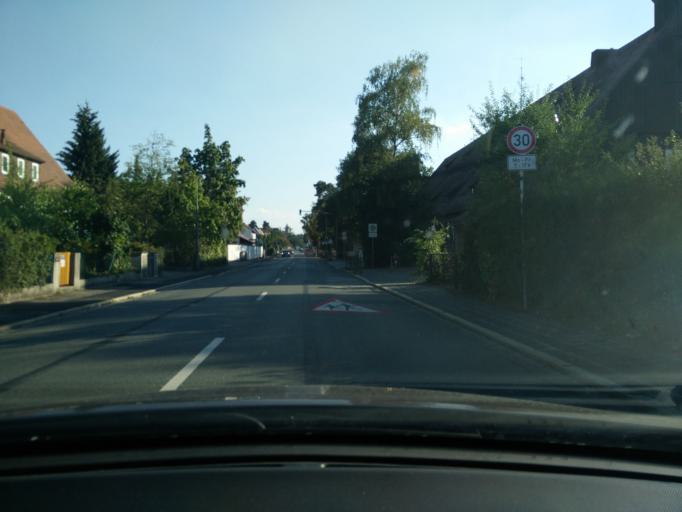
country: DE
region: Bavaria
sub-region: Regierungsbezirk Mittelfranken
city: Nuernberg
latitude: 49.4037
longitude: 11.0869
